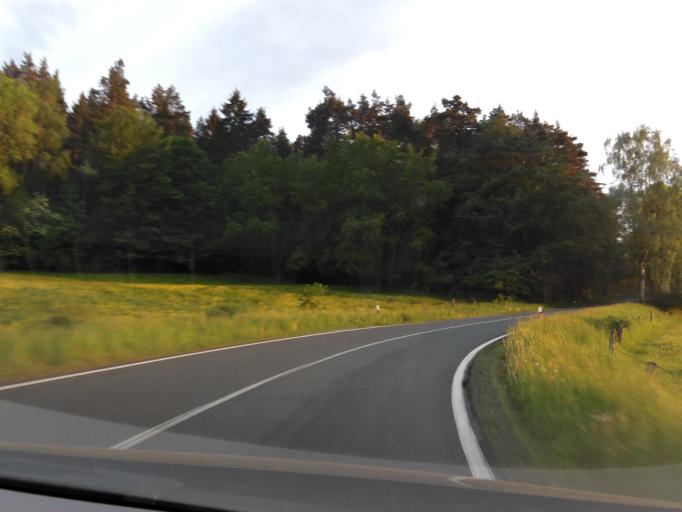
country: DE
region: Thuringia
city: Frauensee
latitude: 50.9010
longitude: 10.1074
